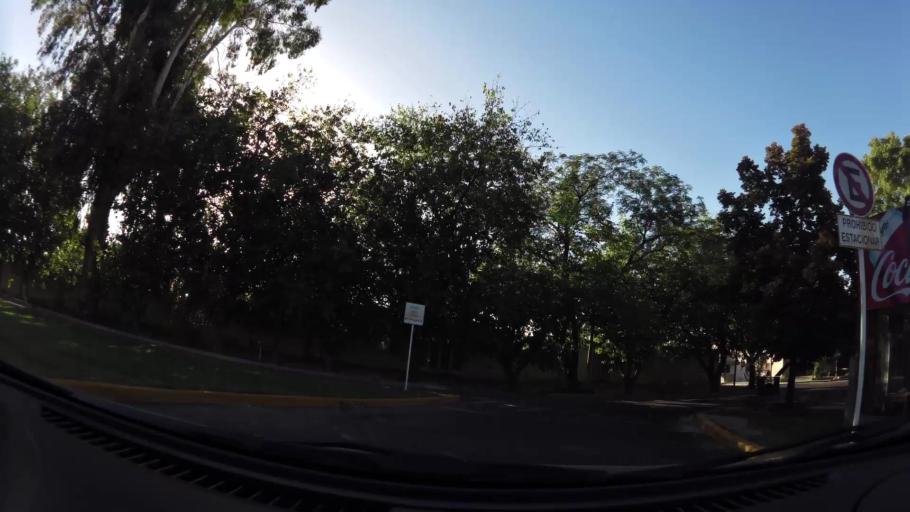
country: AR
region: Mendoza
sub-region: Departamento de Godoy Cruz
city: Godoy Cruz
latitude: -32.9415
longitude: -68.8499
